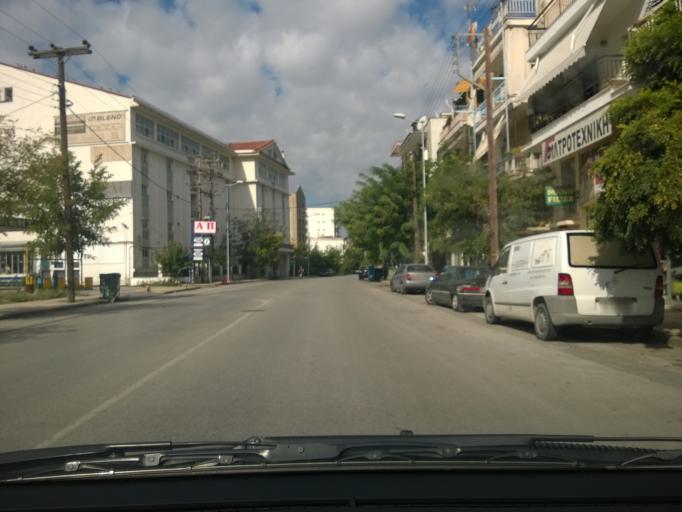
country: GR
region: Central Macedonia
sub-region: Nomos Thessalonikis
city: Ampelokipoi
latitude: 40.6492
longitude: 22.9167
